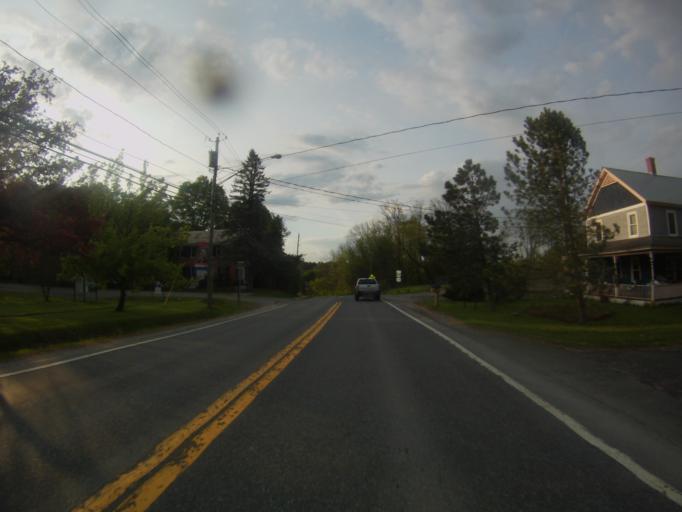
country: US
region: New York
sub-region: Essex County
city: Port Henry
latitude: 43.9522
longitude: -73.4320
